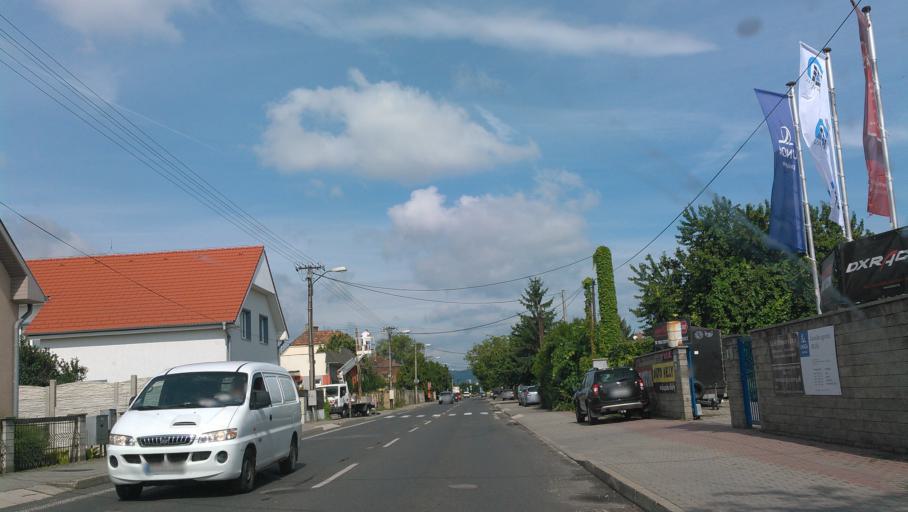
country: SK
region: Bratislavsky
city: Bratislava
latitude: 48.1529
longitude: 17.1982
